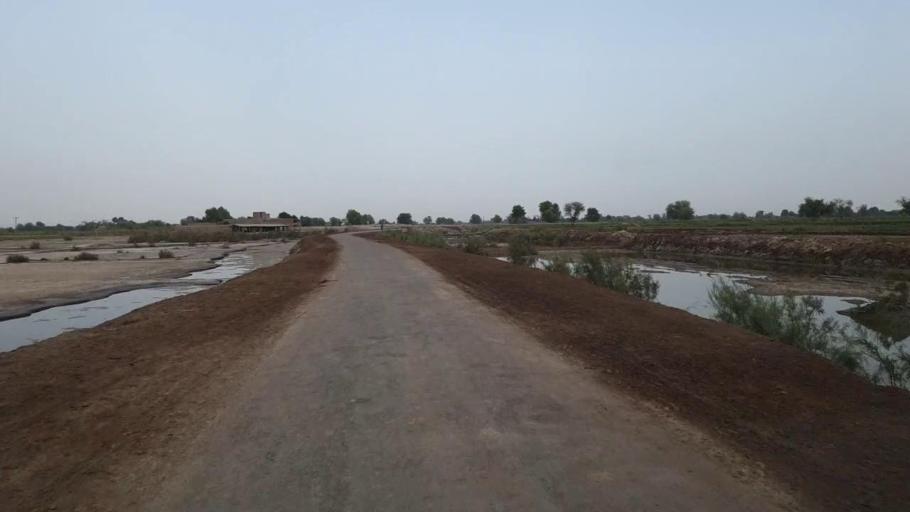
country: PK
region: Sindh
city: Bandhi
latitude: 26.5320
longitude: 68.2135
